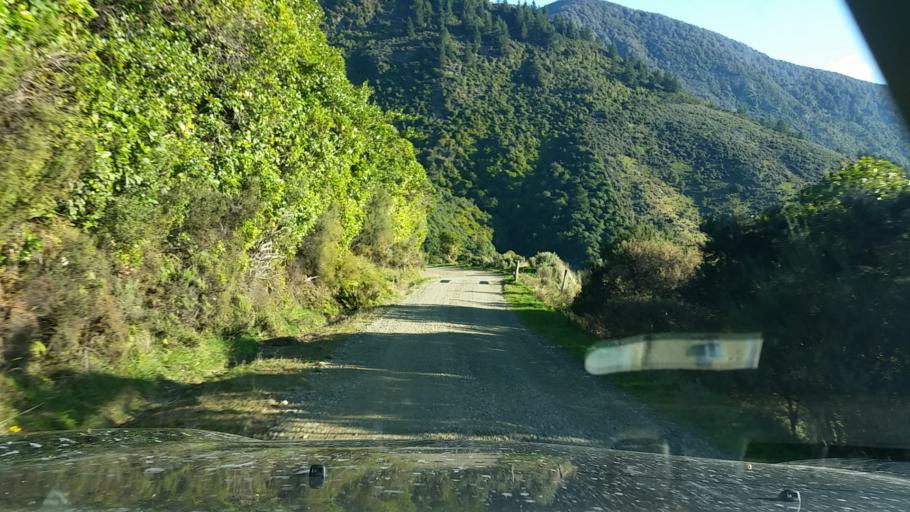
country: NZ
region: Marlborough
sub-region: Marlborough District
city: Picton
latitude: -41.0235
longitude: 174.1551
